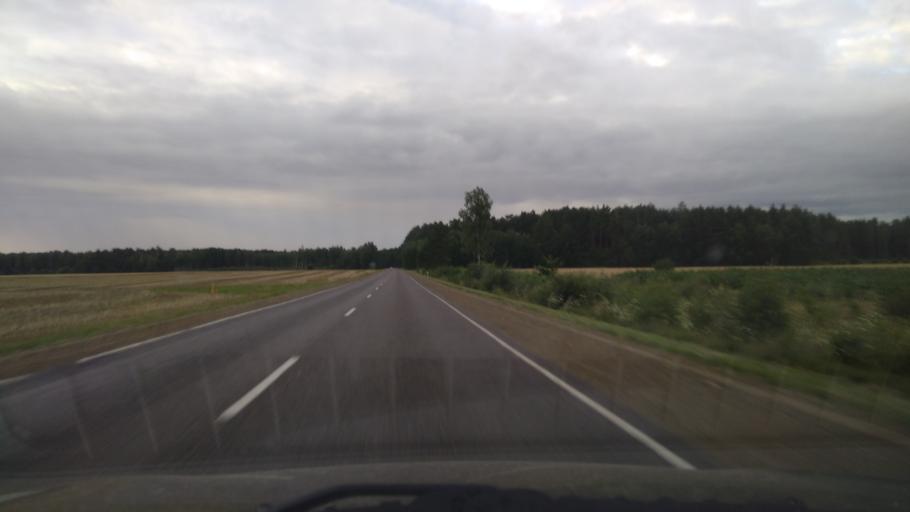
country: BY
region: Brest
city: Byaroza
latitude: 52.4005
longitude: 25.0037
